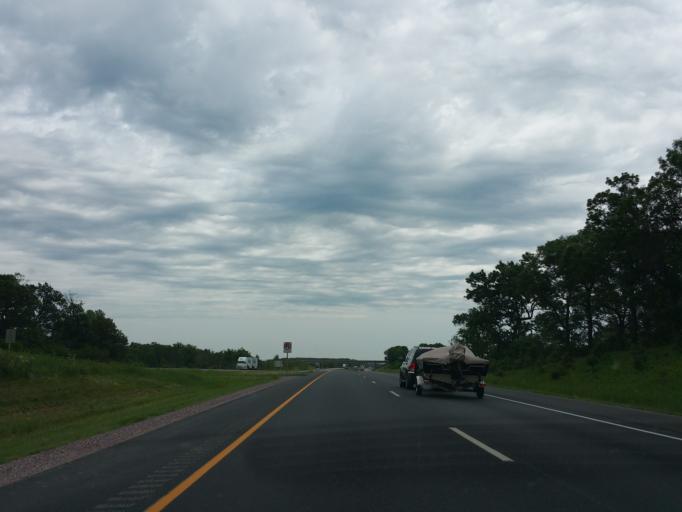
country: US
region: Wisconsin
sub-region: Juneau County
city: Mauston
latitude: 43.7408
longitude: -89.9343
